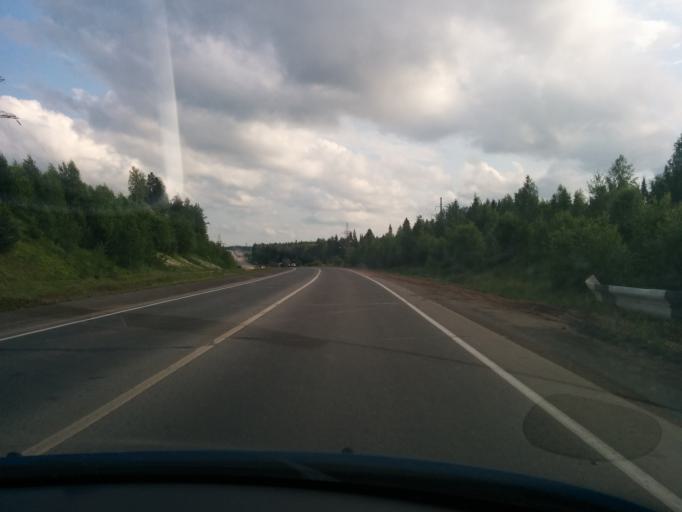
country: RU
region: Perm
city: Novyye Lyady
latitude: 58.0624
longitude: 56.4272
